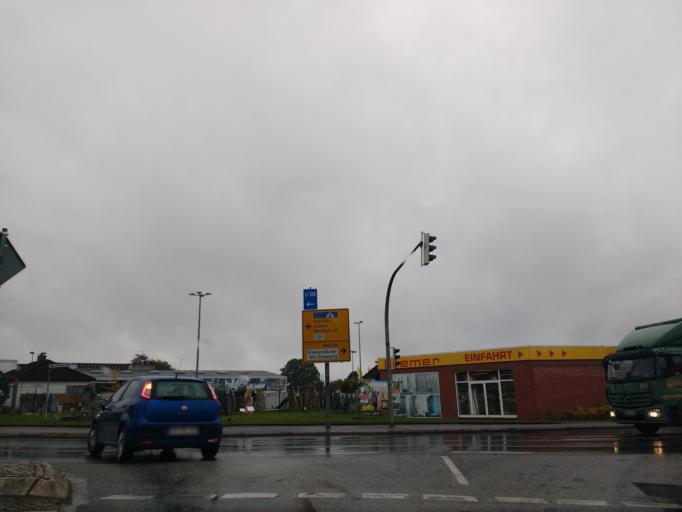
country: DE
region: Schleswig-Holstein
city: Eutin
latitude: 54.1288
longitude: 10.6255
